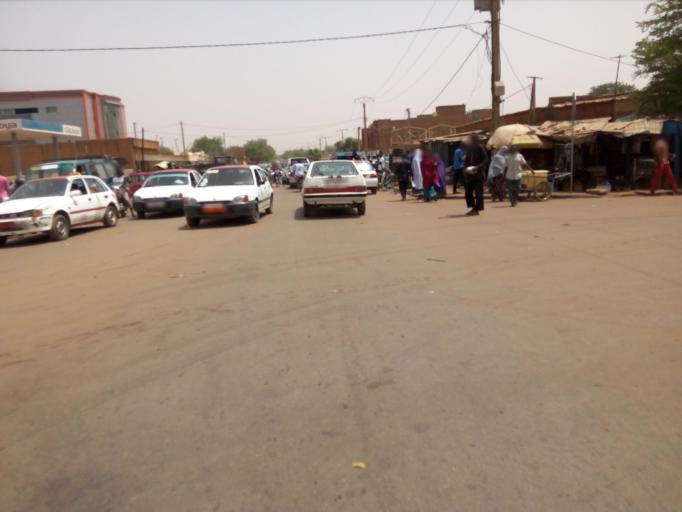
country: NE
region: Niamey
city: Niamey
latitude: 13.5245
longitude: 2.1205
